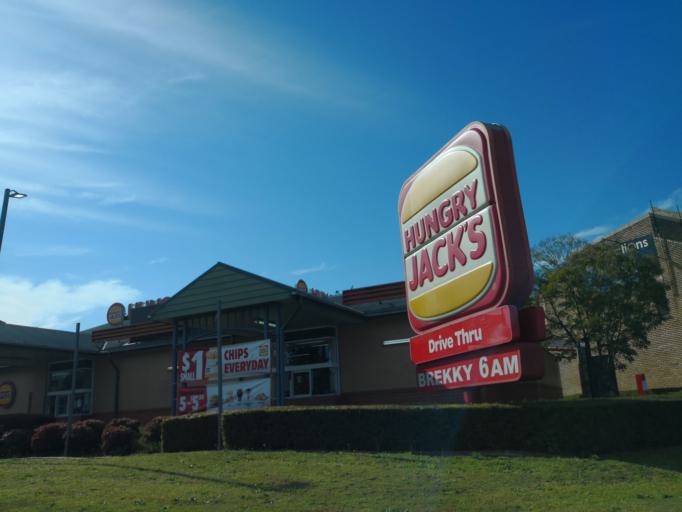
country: AU
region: New South Wales
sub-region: Gosford Shire
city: Narara
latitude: -33.4038
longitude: 151.3505
